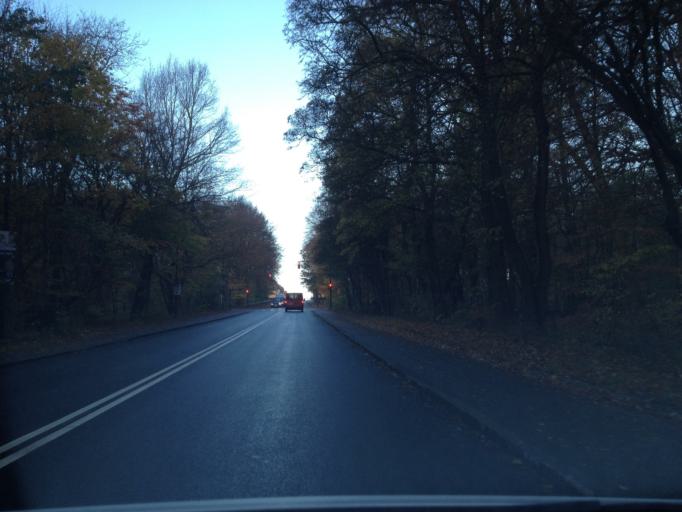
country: DK
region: Capital Region
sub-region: Gentofte Kommune
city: Charlottenlund
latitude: 55.7515
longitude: 12.5774
